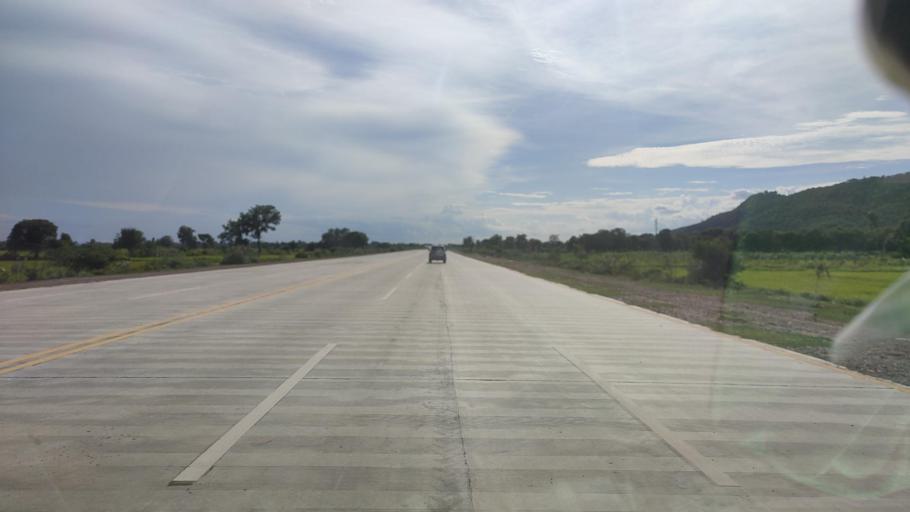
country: MM
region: Mandalay
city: Kyaukse
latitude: 21.5978
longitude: 96.1708
